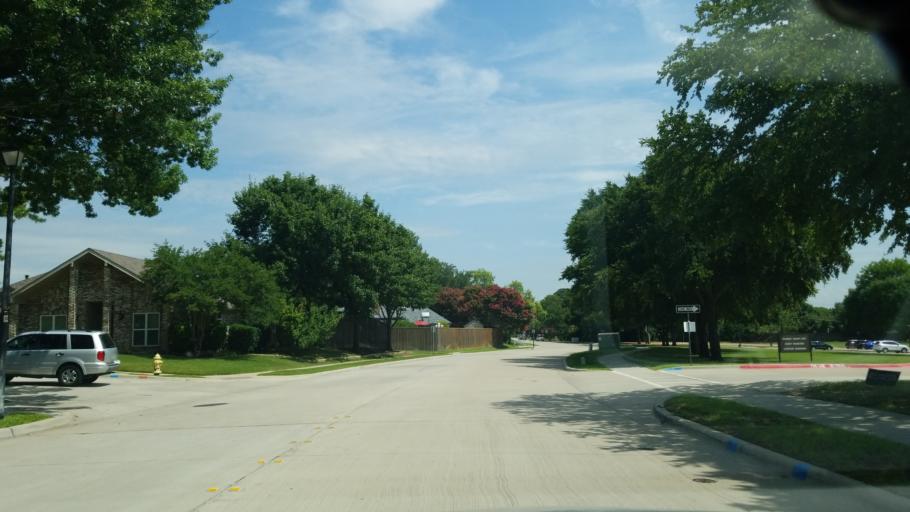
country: US
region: Texas
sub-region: Dallas County
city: Coppell
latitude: 32.9622
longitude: -96.9705
